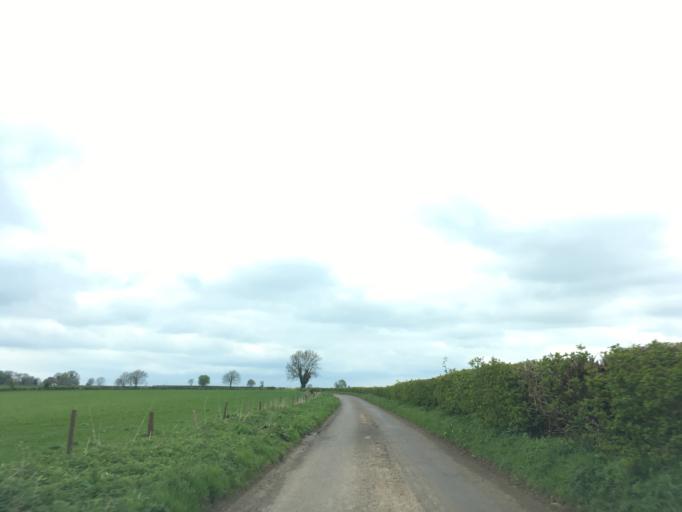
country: GB
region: England
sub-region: Gloucestershire
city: Wotton-under-Edge
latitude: 51.6592
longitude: -2.2982
